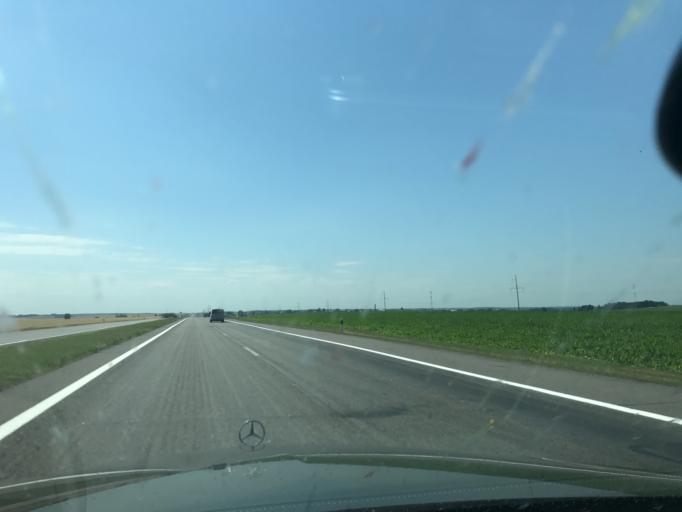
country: BY
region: Minsk
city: Haradzyeya
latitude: 53.3610
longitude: 26.4760
